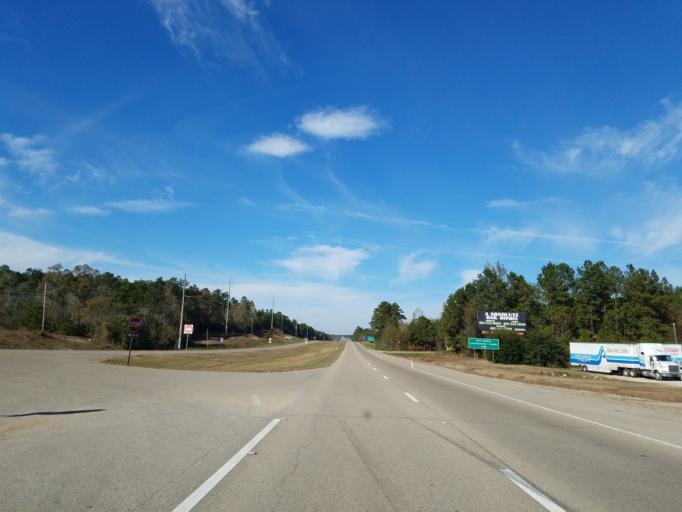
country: US
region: Mississippi
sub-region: Forrest County
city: Hattiesburg
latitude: 31.2508
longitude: -89.2781
